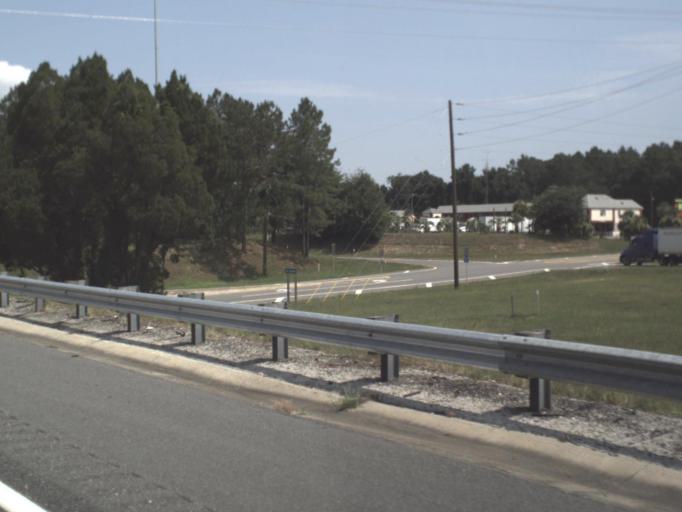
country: US
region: Florida
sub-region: Hamilton County
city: Jasper
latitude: 30.5178
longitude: -83.0577
